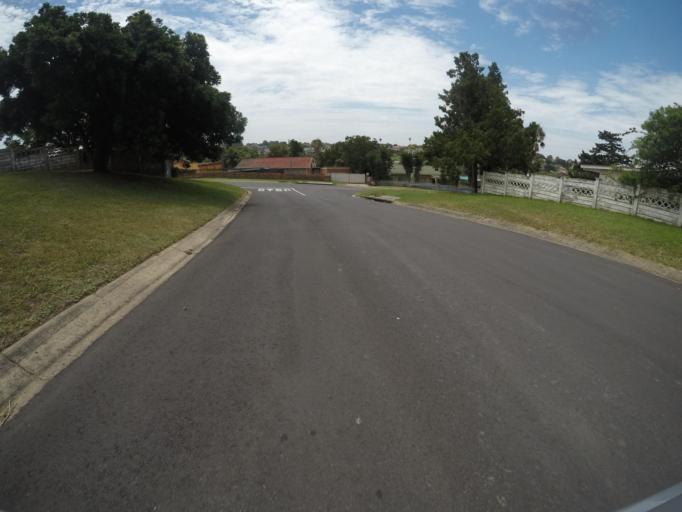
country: ZA
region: Eastern Cape
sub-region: Buffalo City Metropolitan Municipality
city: East London
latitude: -32.9820
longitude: 27.8681
